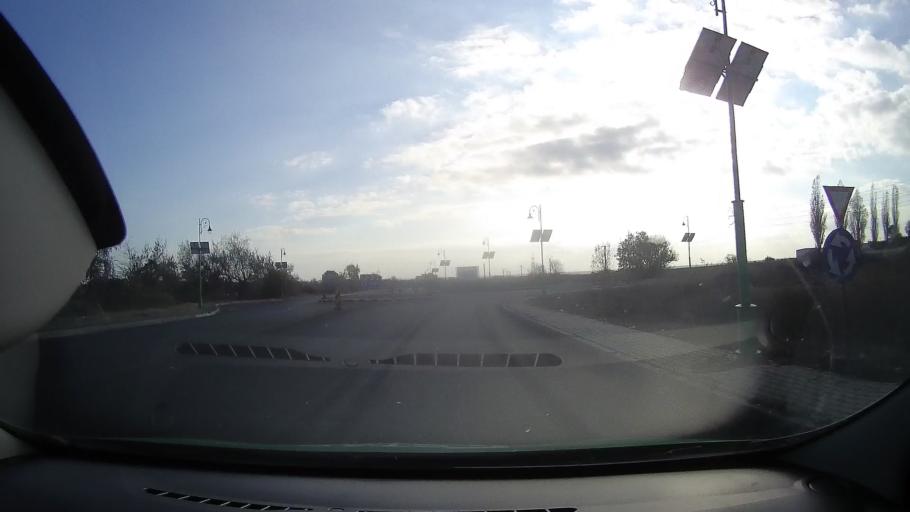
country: RO
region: Constanta
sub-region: Comuna Navodari
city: Navodari
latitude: 44.2980
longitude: 28.6136
